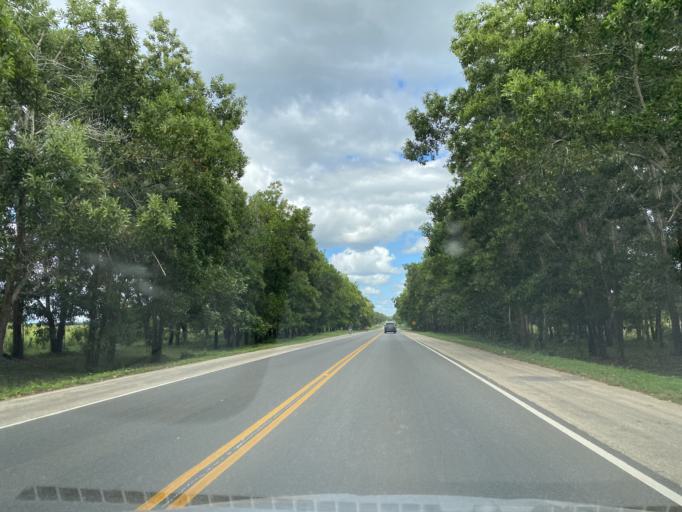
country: DO
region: Santo Domingo
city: Guerra
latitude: 18.6410
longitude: -69.7555
